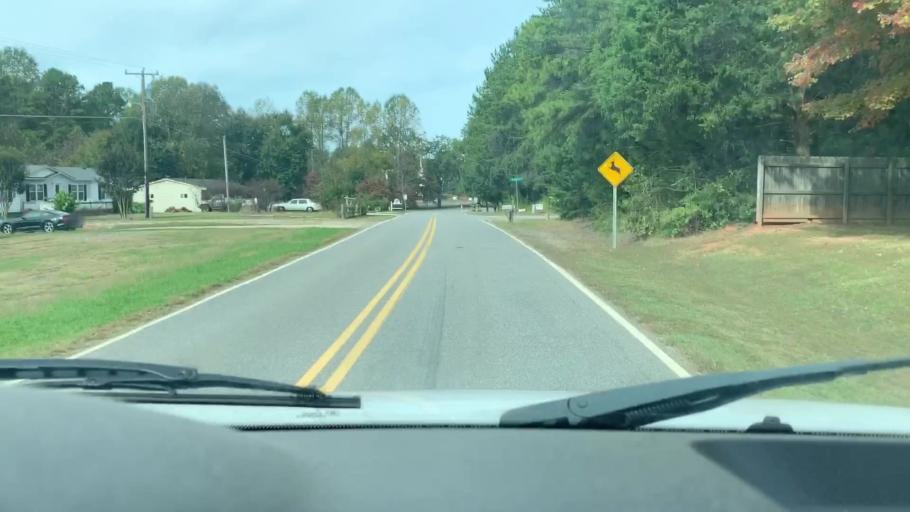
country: US
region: North Carolina
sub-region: Catawba County
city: Lake Norman of Catawba
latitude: 35.5653
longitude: -80.9278
